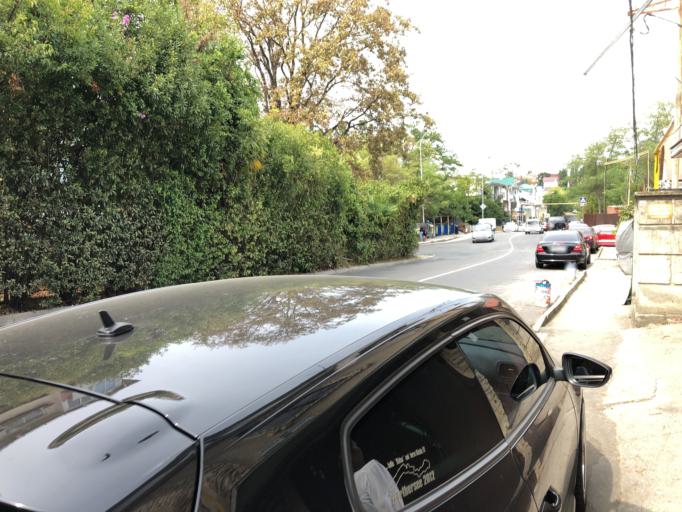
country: RU
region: Krasnodarskiy
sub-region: Sochi City
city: Sochi
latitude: 43.5932
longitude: 39.7418
